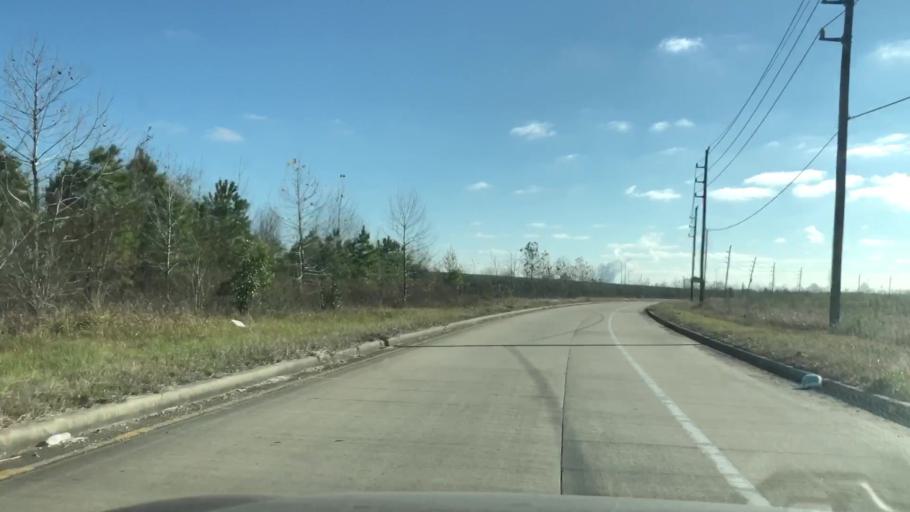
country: US
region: Texas
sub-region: Harris County
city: Cloverleaf
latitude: 29.8300
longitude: -95.1780
